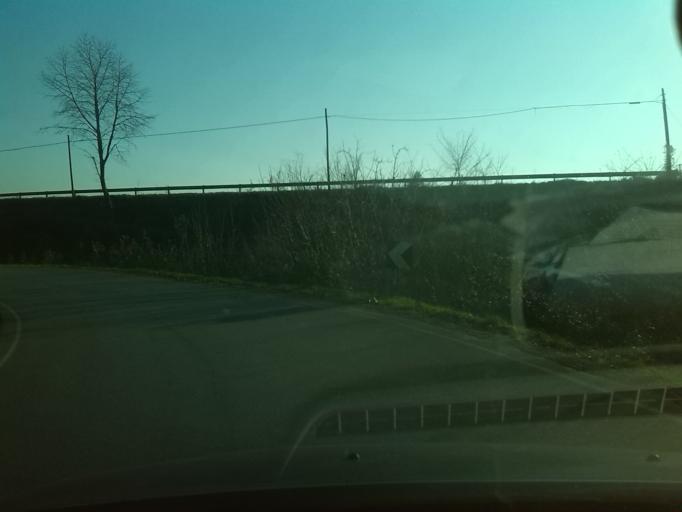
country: IT
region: Friuli Venezia Giulia
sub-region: Provincia di Udine
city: Santa Maria la Longa
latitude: 45.9188
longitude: 13.2782
